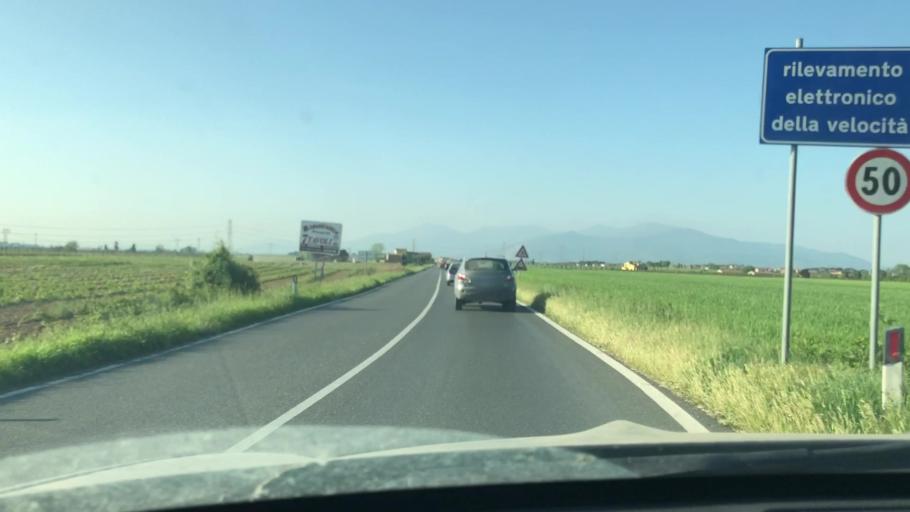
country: IT
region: Tuscany
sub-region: Province of Pisa
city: Cenaia
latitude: 43.5912
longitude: 10.5297
